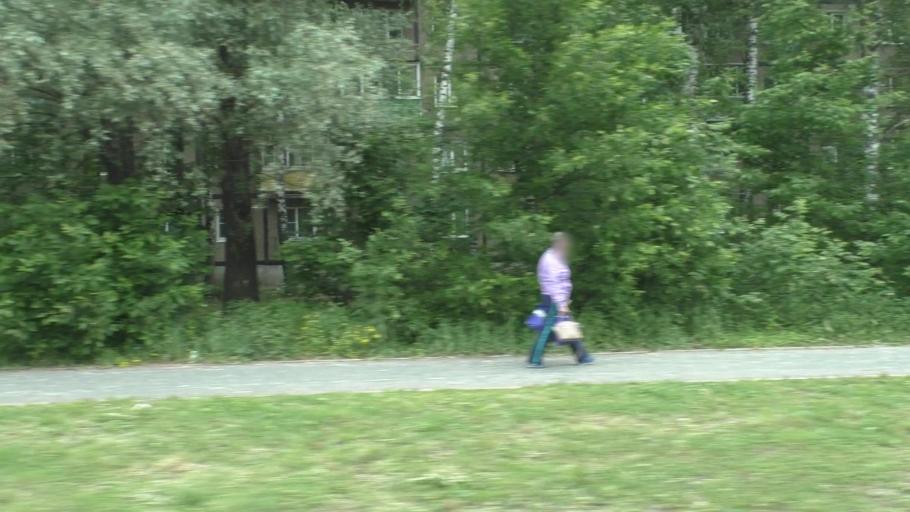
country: RU
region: Moskovskaya
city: Yegor'yevsk
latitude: 55.3695
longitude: 39.0529
